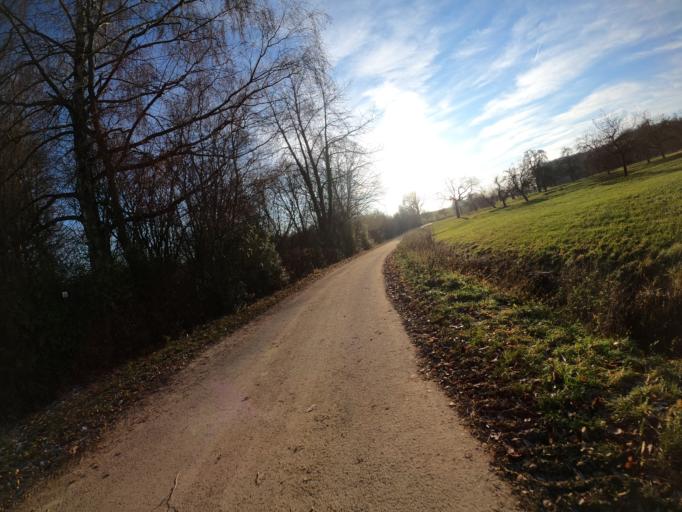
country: DE
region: Baden-Wuerttemberg
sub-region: Regierungsbezirk Stuttgart
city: Boll
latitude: 48.6593
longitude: 9.6095
